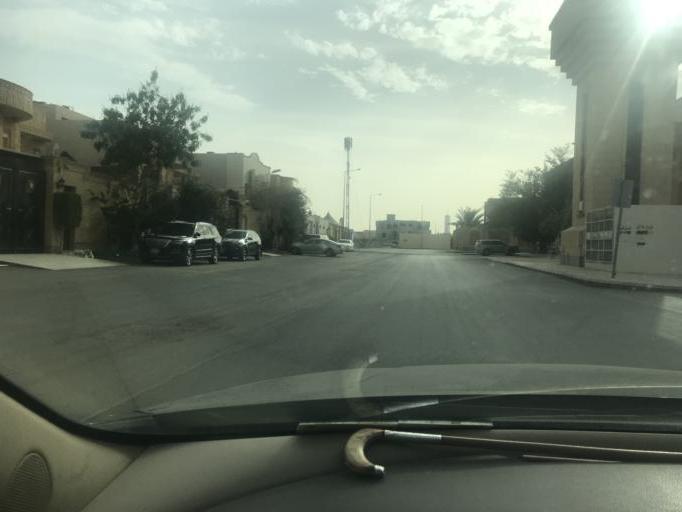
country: SA
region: Ar Riyad
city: Riyadh
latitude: 24.8064
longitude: 46.6692
